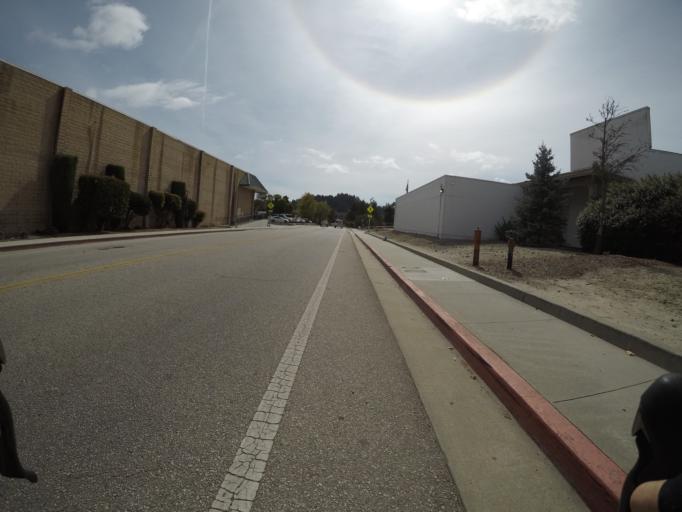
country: US
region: California
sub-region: Santa Cruz County
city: Scotts Valley
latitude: 37.0482
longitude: -122.0282
